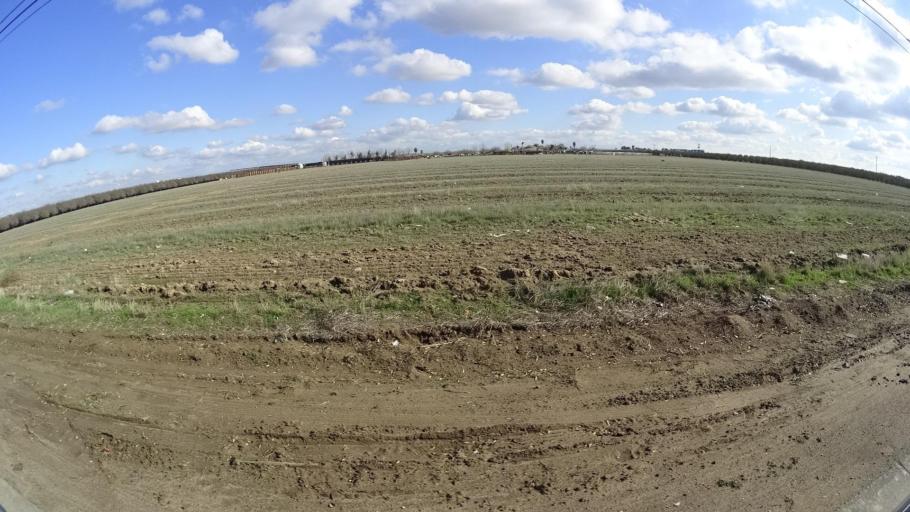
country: US
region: California
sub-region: Kern County
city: McFarland
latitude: 35.7090
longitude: -119.2408
